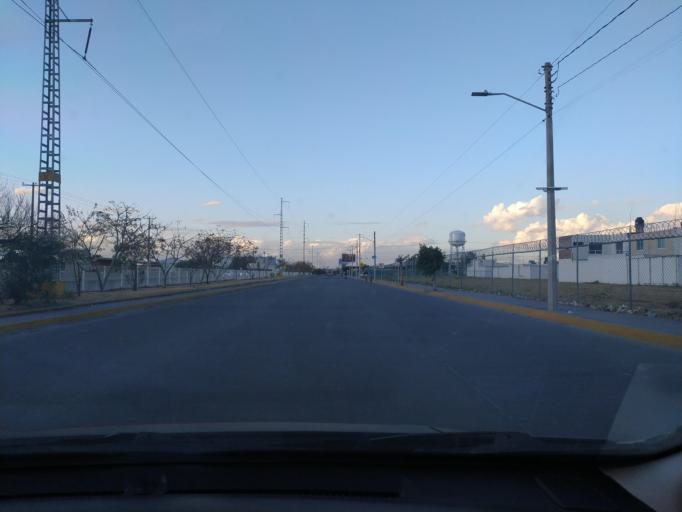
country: LA
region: Oudomxai
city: Muang La
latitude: 21.0178
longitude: 101.8697
